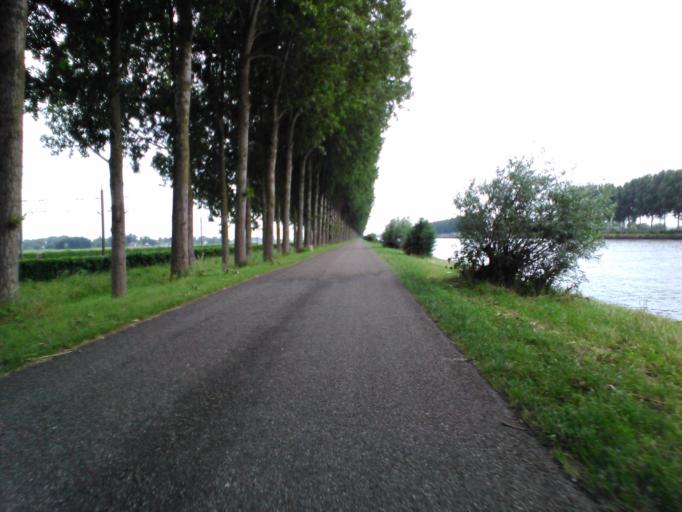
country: NL
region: Utrecht
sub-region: Stichtse Vecht
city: Vreeland
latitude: 52.2297
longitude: 5.0068
